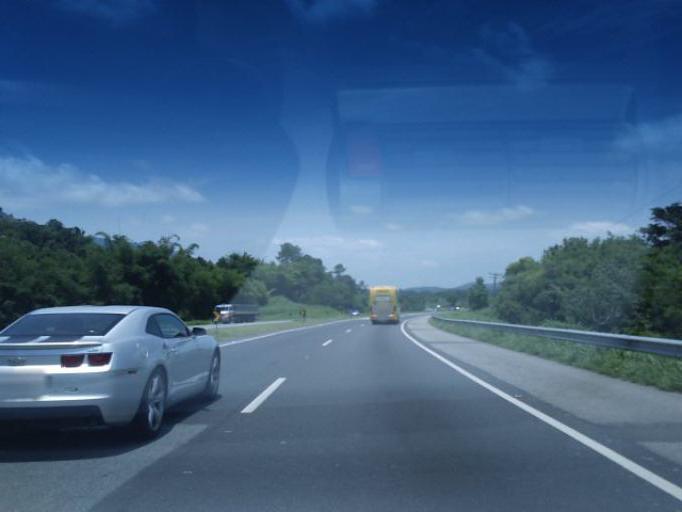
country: BR
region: Sao Paulo
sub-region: Miracatu
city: Miracatu
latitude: -24.2795
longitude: -47.4234
